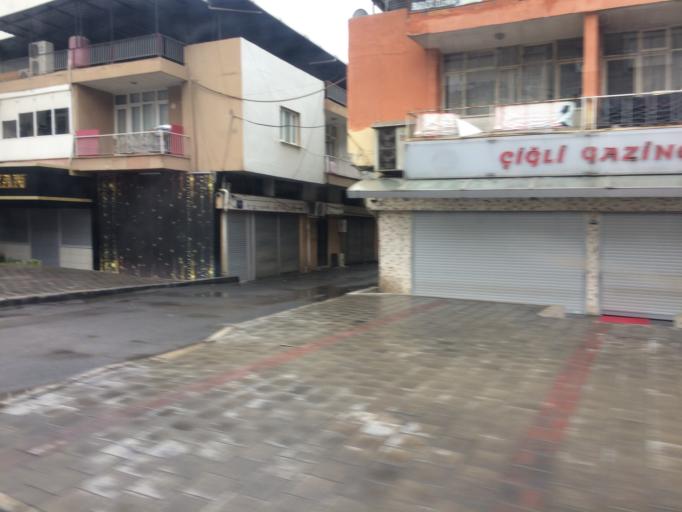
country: TR
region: Izmir
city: Karsiyaka
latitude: 38.4982
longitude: 27.0572
